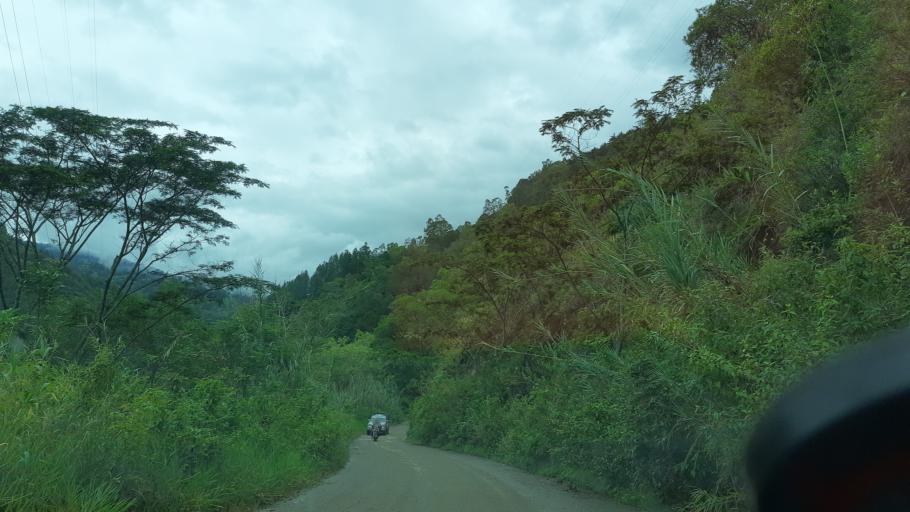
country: CO
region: Cundinamarca
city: Tenza
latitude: 5.0751
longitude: -73.4003
